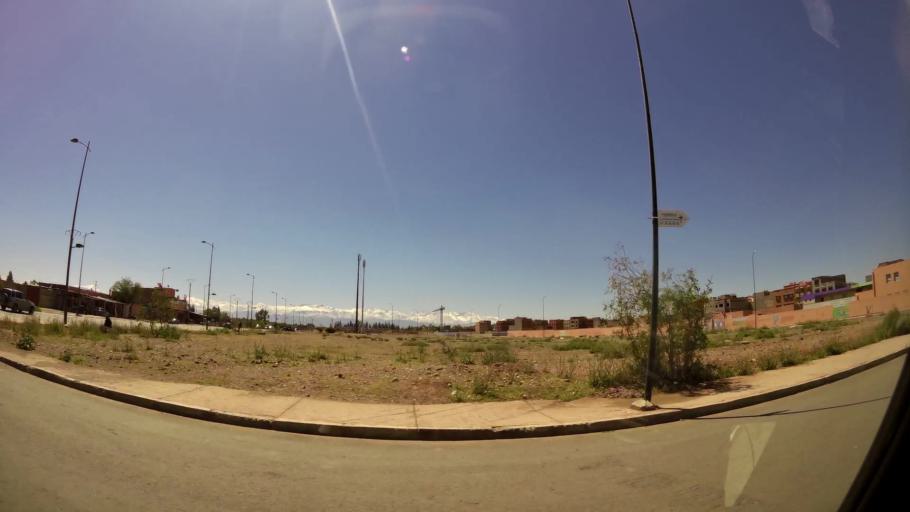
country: MA
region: Marrakech-Tensift-Al Haouz
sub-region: Marrakech
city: Marrakesh
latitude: 31.5550
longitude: -7.9764
